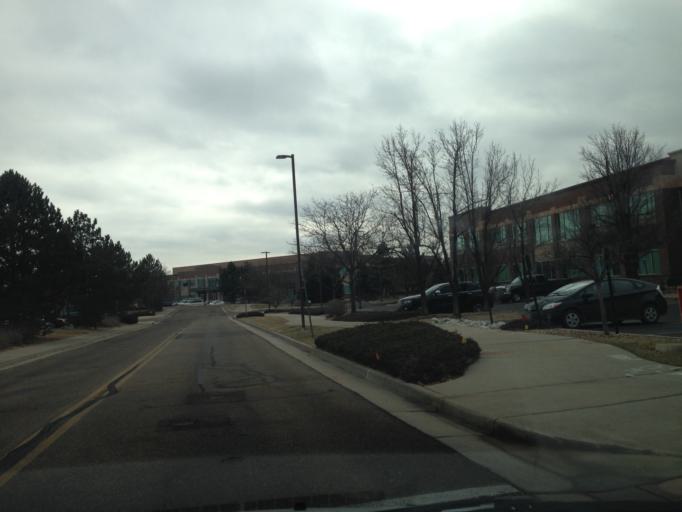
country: US
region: Colorado
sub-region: Boulder County
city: Superior
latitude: 39.9576
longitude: -105.1603
